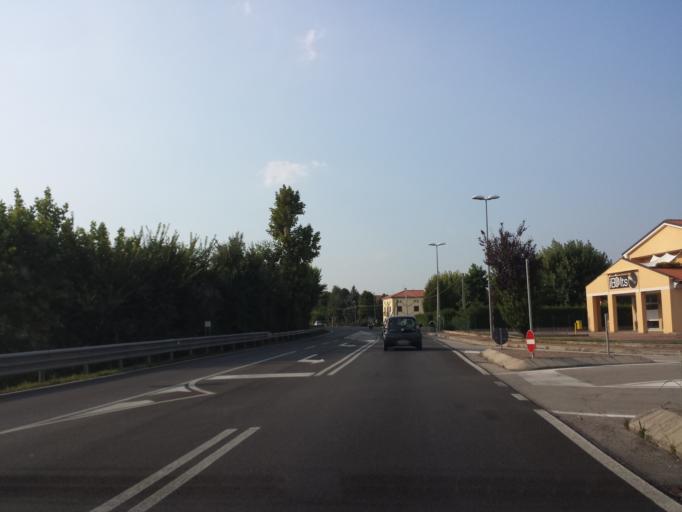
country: IT
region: Veneto
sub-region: Provincia di Padova
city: Arlesega
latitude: 45.4647
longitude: 11.7145
